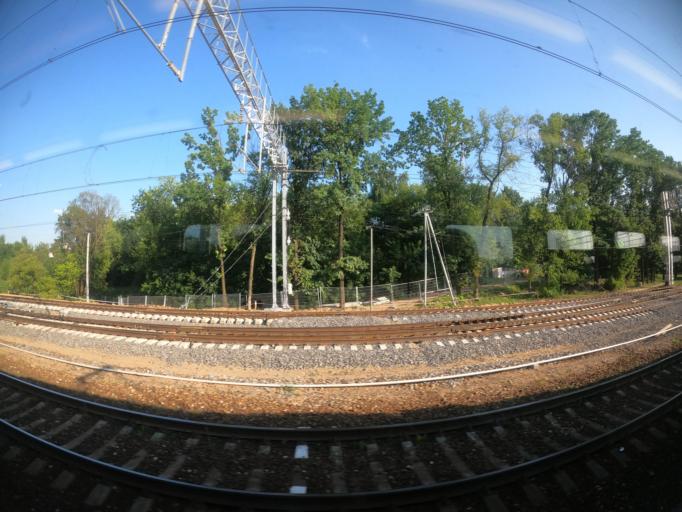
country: RU
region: Moscow
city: Solntsevo
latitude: 55.6587
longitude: 37.3902
